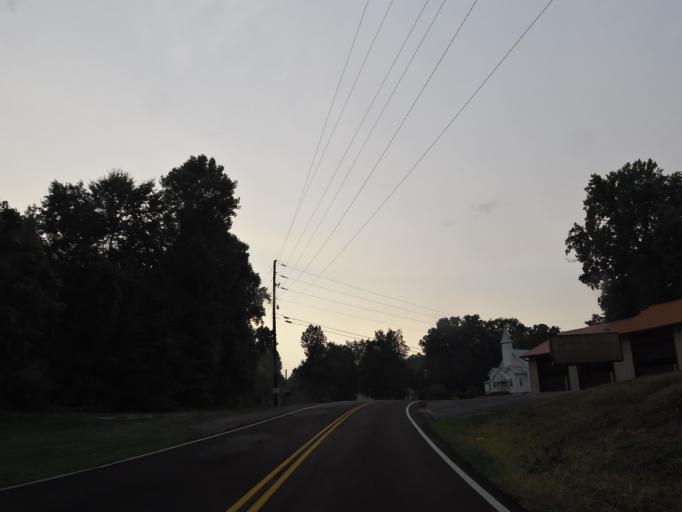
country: US
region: Tennessee
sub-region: Sevier County
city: Seymour
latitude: 35.8248
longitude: -83.7040
